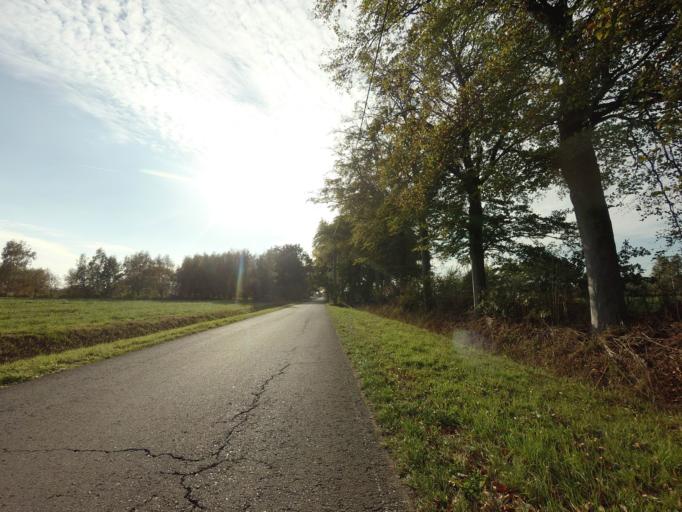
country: BE
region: Flanders
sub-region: Provincie Antwerpen
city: Stabroek
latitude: 51.3492
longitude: 4.3618
